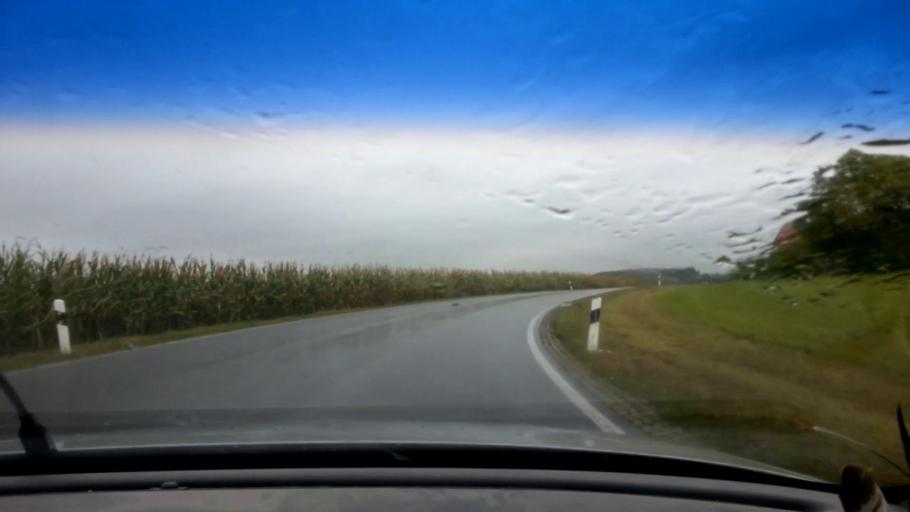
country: DE
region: Bavaria
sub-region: Upper Franconia
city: Poxdorf
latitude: 49.9082
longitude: 11.1447
